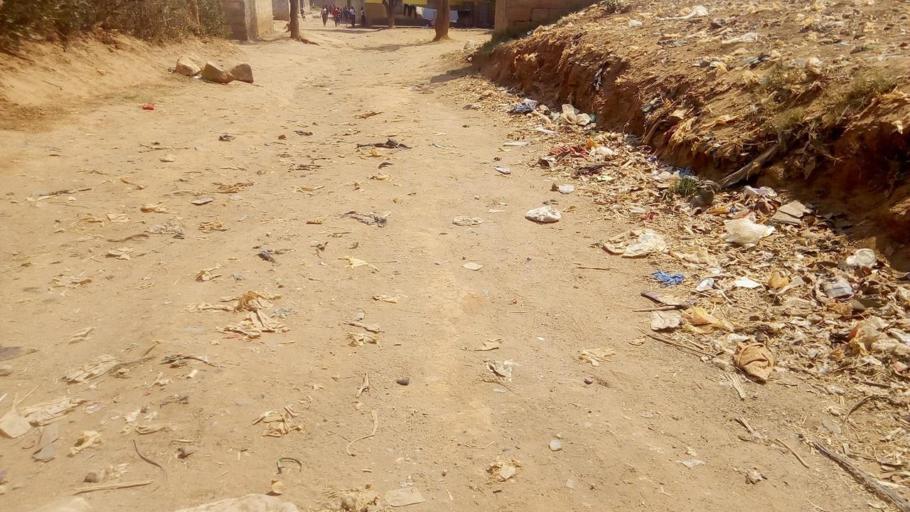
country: ZM
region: Lusaka
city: Lusaka
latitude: -15.3579
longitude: 28.2974
